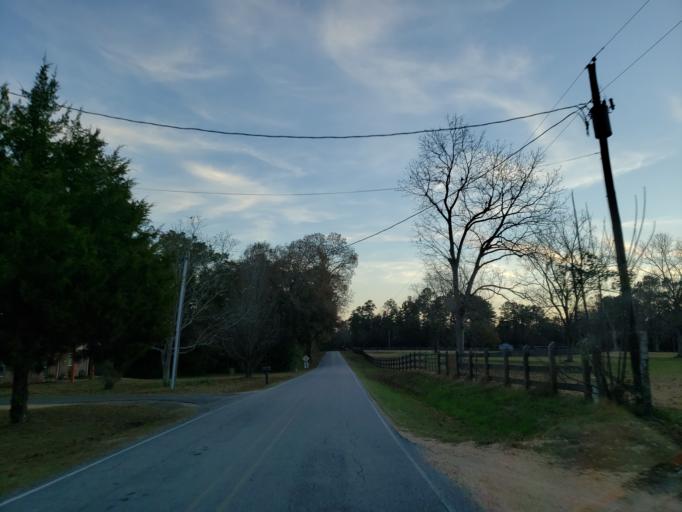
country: US
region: Mississippi
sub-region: Forrest County
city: Hattiesburg
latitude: 31.2439
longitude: -89.3139
